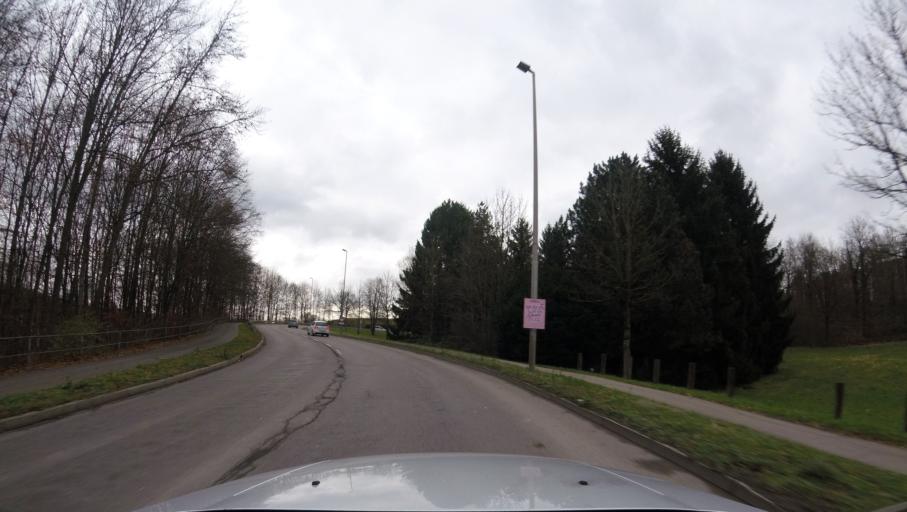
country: DE
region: Baden-Wuerttemberg
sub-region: Regierungsbezirk Stuttgart
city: Backnang
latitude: 48.9461
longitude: 9.4372
